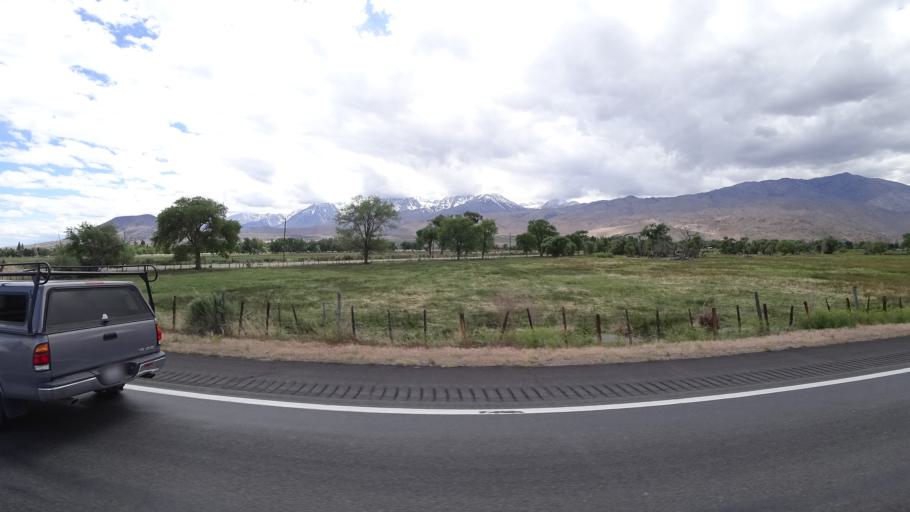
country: US
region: California
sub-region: Inyo County
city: Big Pine
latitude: 37.1743
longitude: -118.2911
